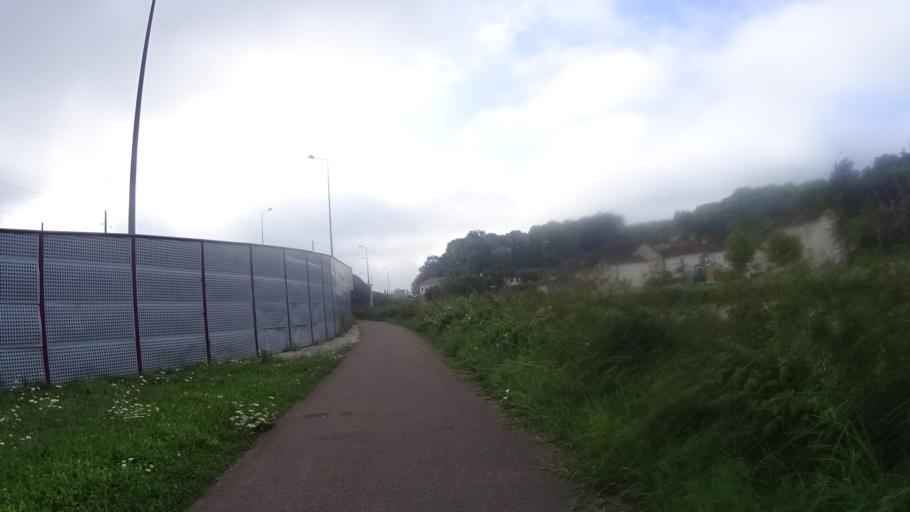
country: FR
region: Lorraine
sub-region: Departement de la Meuse
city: Fains-Veel
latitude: 48.7880
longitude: 5.1383
